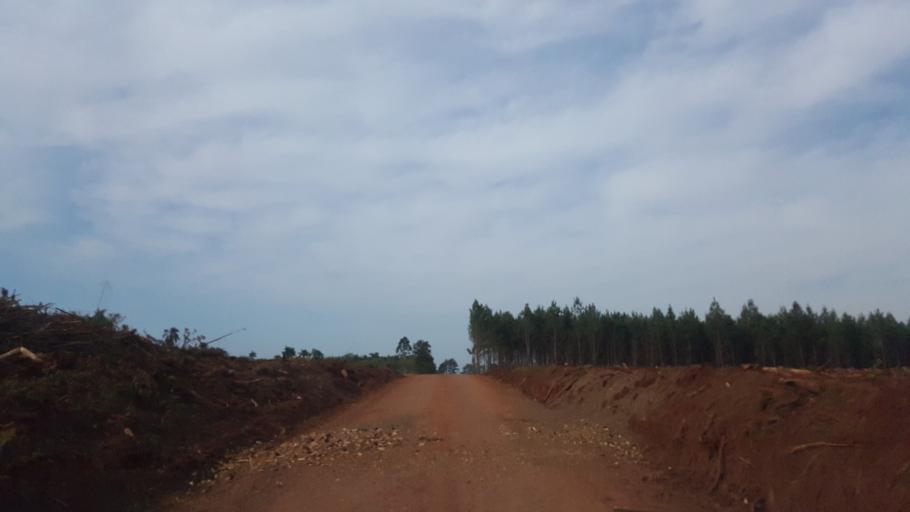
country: AR
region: Misiones
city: Capiovi
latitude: -26.9193
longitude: -55.1165
